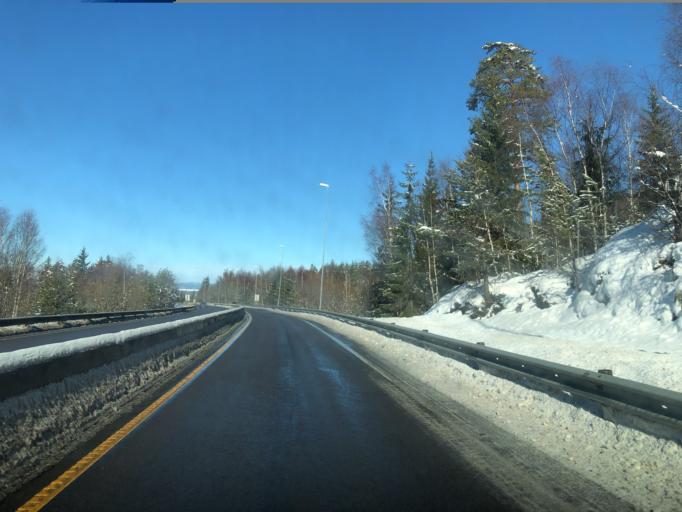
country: NO
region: Buskerud
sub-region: Hole
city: Vik
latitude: 60.0319
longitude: 10.2711
